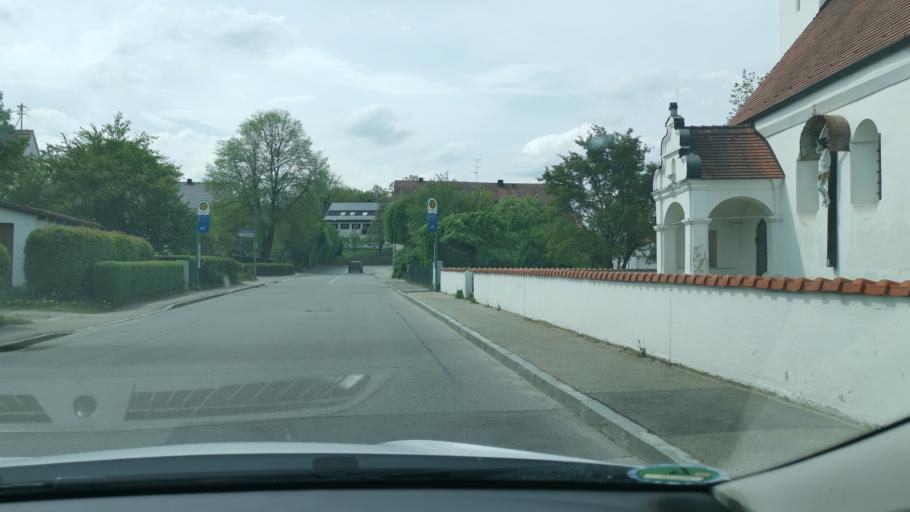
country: DE
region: Bavaria
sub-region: Upper Bavaria
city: Petershausen
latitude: 48.3928
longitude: 11.4857
